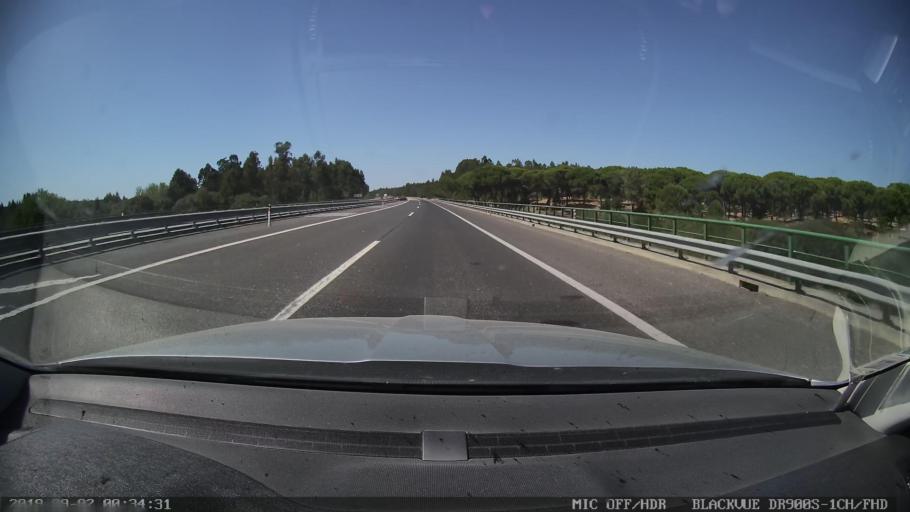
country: PT
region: Evora
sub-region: Vendas Novas
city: Vendas Novas
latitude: 38.6335
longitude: -8.5381
